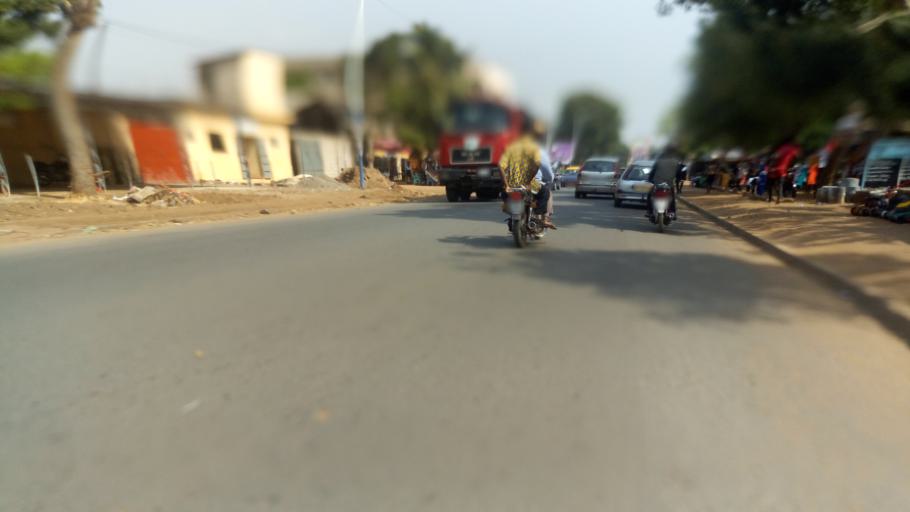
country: TG
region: Maritime
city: Lome
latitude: 6.1714
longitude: 1.1905
